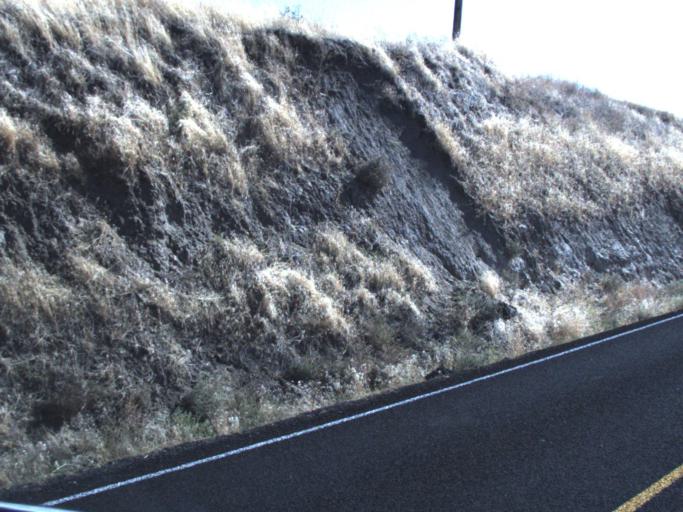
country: US
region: Washington
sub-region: Walla Walla County
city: Waitsburg
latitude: 46.2689
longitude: -118.3509
